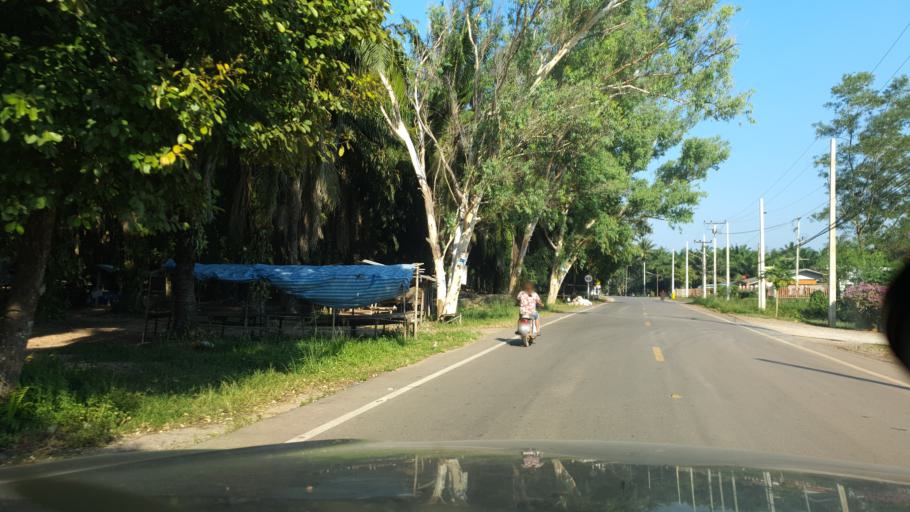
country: TH
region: Chumphon
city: Pathio
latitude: 10.7487
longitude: 99.3304
